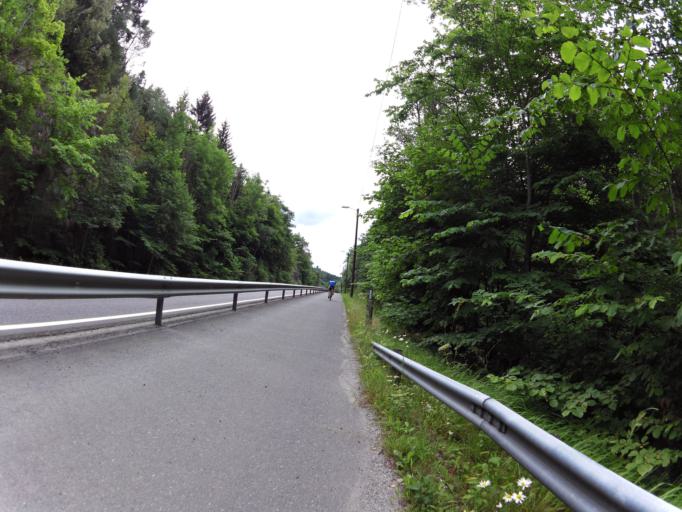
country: NO
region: Akershus
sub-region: As
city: As
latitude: 59.7126
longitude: 10.7344
